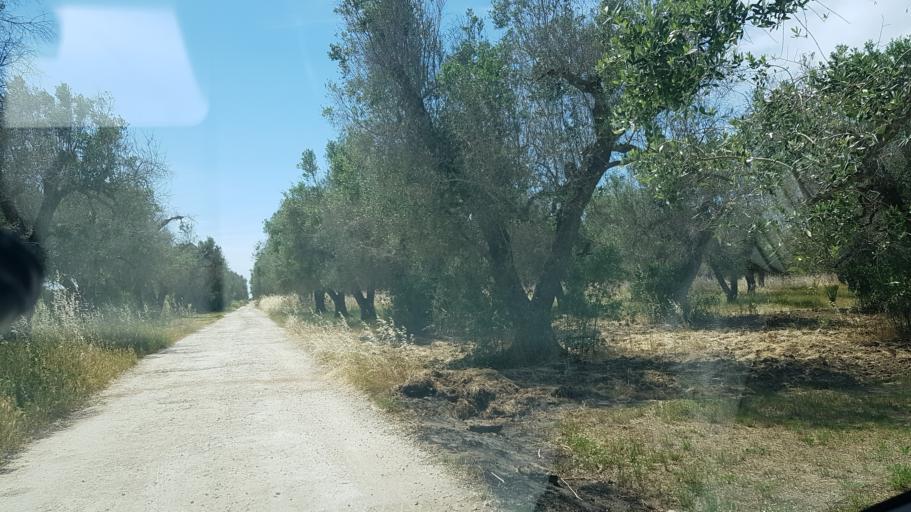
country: IT
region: Apulia
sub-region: Provincia di Brindisi
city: Tuturano
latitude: 40.5422
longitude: 17.9971
